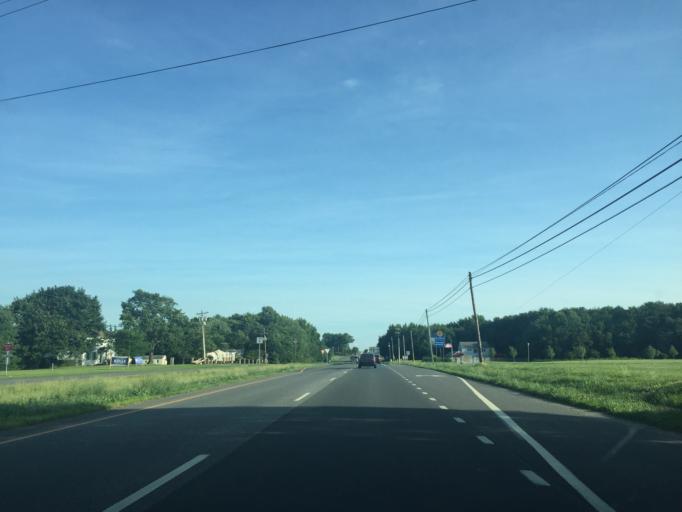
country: US
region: Delaware
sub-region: Kent County
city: Smyrna
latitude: 39.2629
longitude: -75.5866
